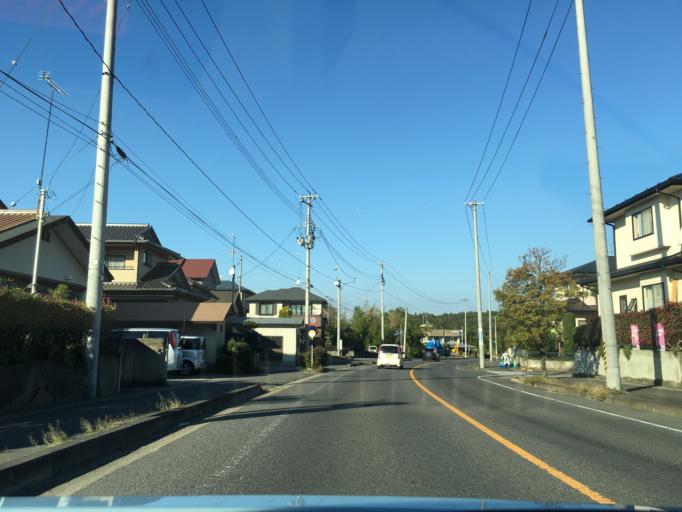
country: JP
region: Fukushima
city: Sukagawa
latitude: 37.3051
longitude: 140.3715
